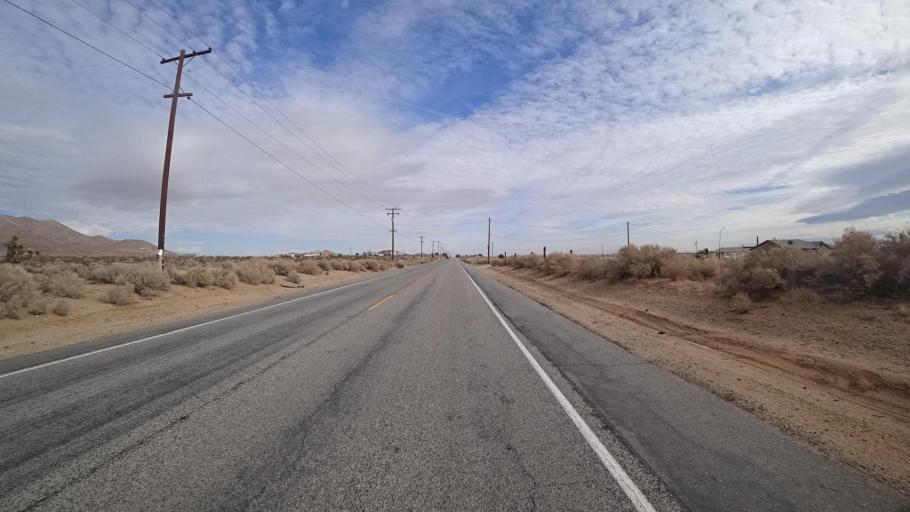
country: US
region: California
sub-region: Kern County
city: Rosamond
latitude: 34.8636
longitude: -118.2873
